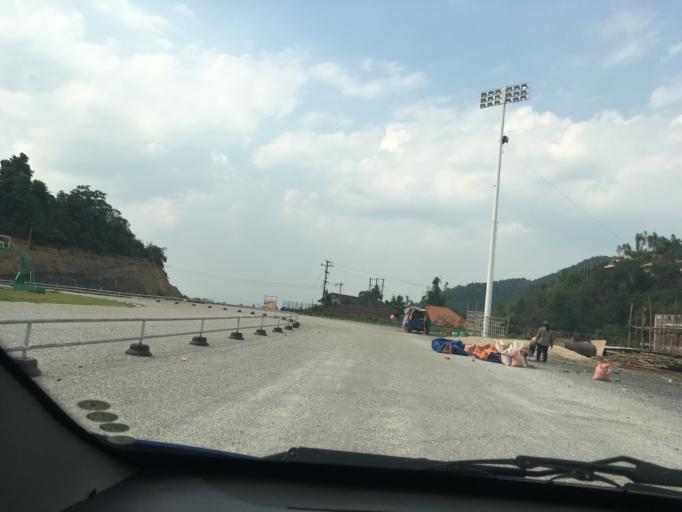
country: LA
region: Phongsali
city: Phongsali
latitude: 21.6827
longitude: 102.0996
